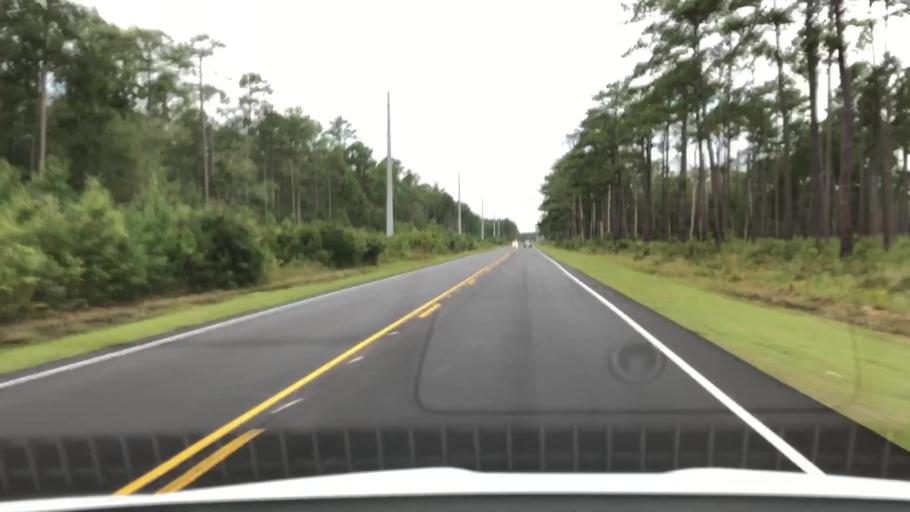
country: US
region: North Carolina
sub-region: Onslow County
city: Swansboro
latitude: 34.7763
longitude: -77.1014
